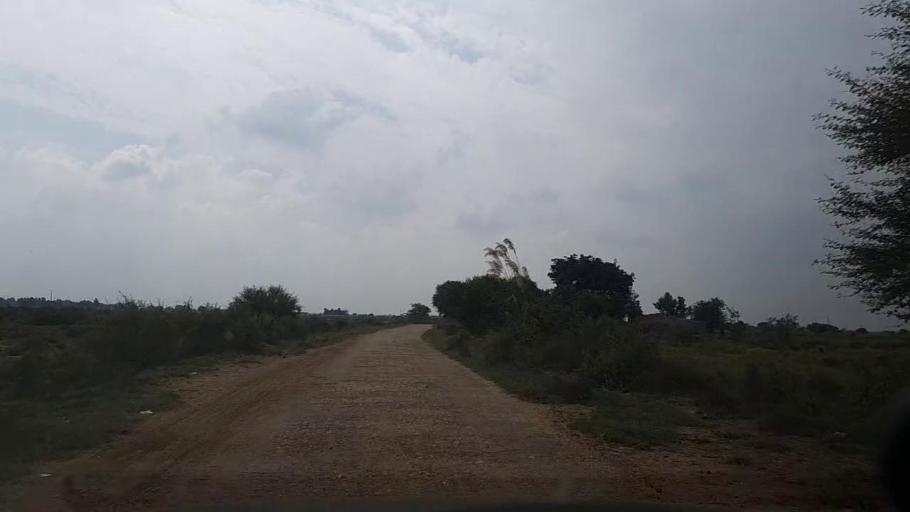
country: PK
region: Sindh
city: Mirpur Batoro
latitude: 24.5887
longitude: 68.1239
